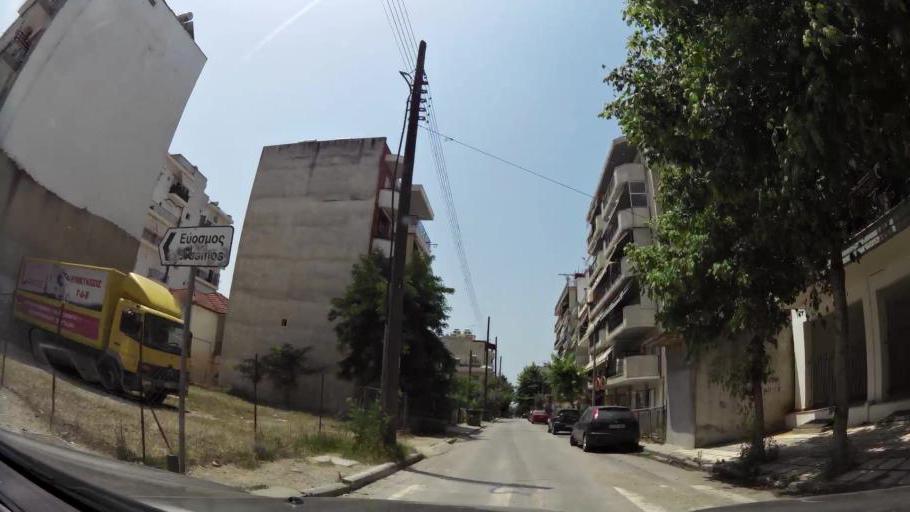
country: GR
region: Central Macedonia
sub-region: Nomos Thessalonikis
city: Menemeni
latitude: 40.6716
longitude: 22.8907
